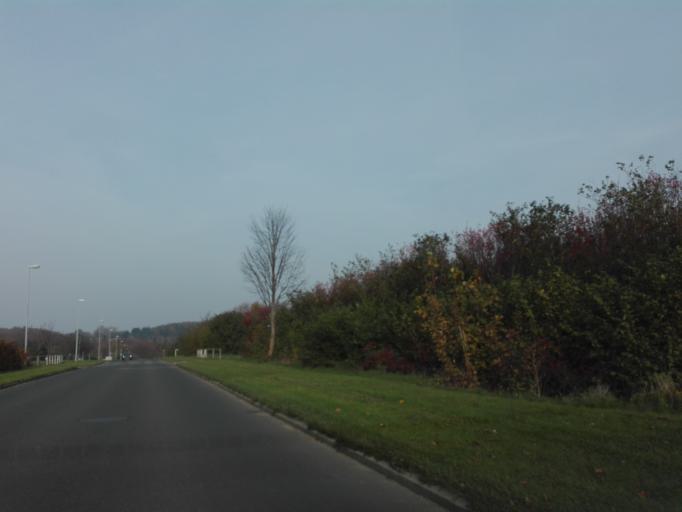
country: DK
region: Central Jutland
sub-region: Odder Kommune
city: Odder
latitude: 55.9795
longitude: 10.1341
